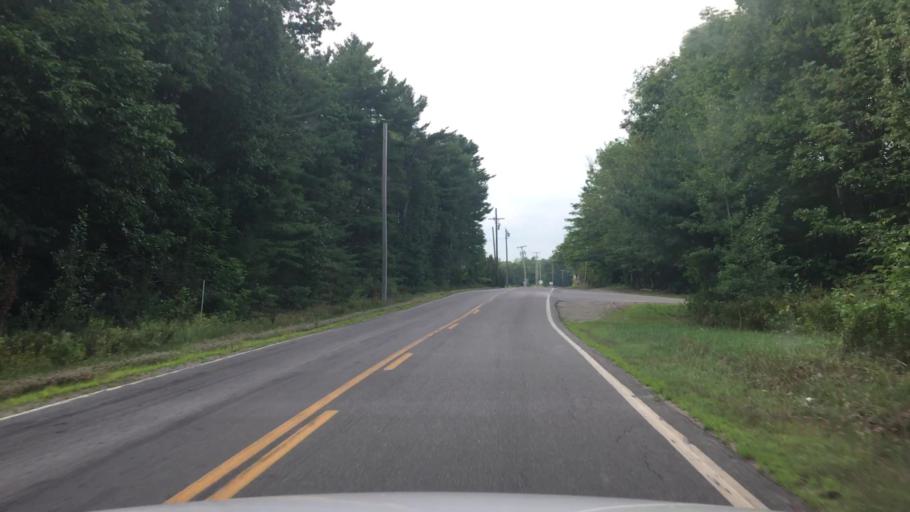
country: US
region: Maine
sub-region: Knox County
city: Washington
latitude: 44.2243
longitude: -69.3872
